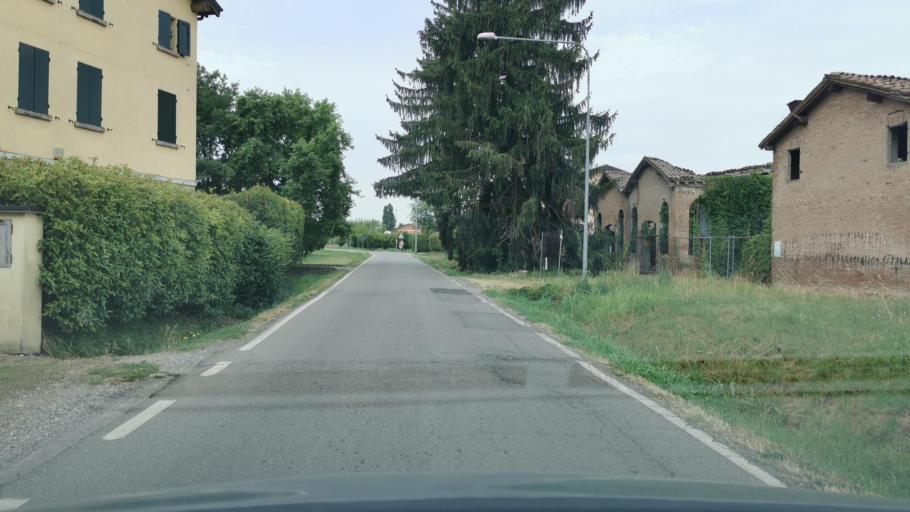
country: IT
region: Emilia-Romagna
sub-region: Provincia di Modena
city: Campogalliano
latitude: 44.6830
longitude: 10.8809
